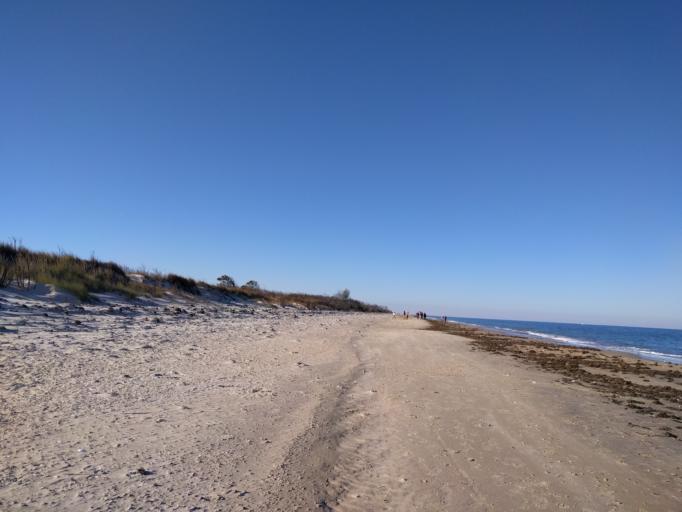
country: US
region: Virginia
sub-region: City of Poquoson
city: Poquoson
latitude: 37.0930
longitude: -76.2737
